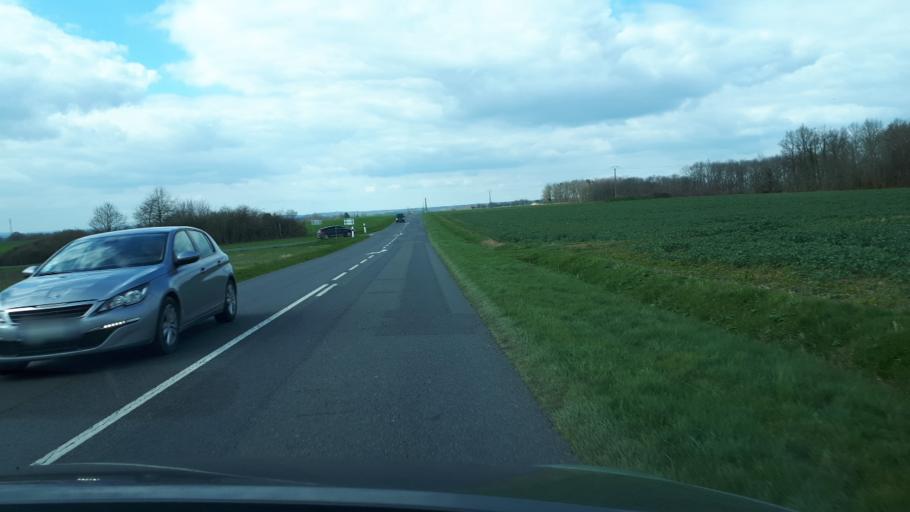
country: FR
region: Centre
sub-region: Departement du Loir-et-Cher
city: Lunay
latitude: 47.7631
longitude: 0.9374
